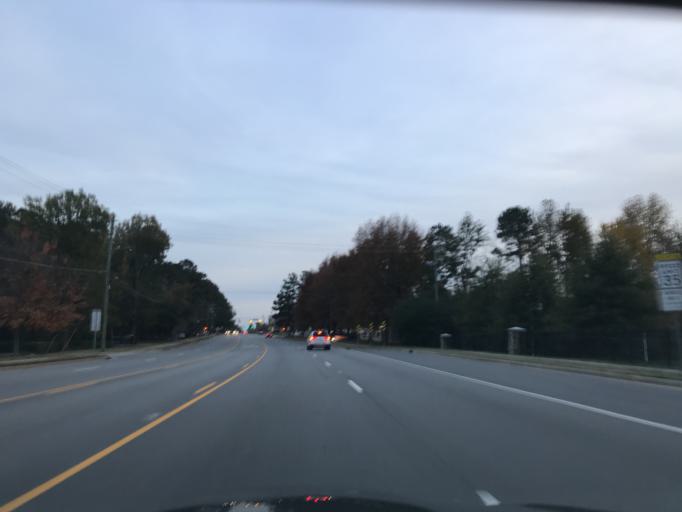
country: US
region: North Carolina
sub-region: Wake County
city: West Raleigh
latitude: 35.8832
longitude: -78.6266
